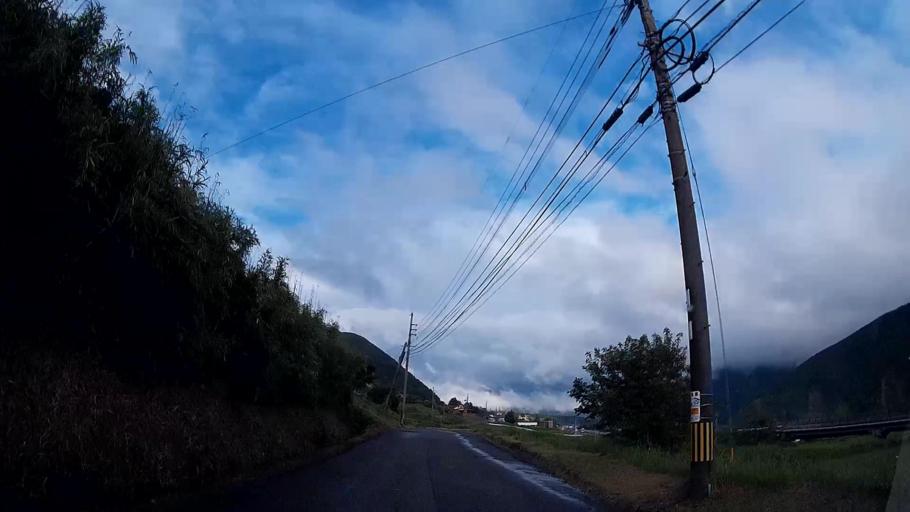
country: JP
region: Kumamoto
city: Ozu
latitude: 32.8798
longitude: 130.9610
